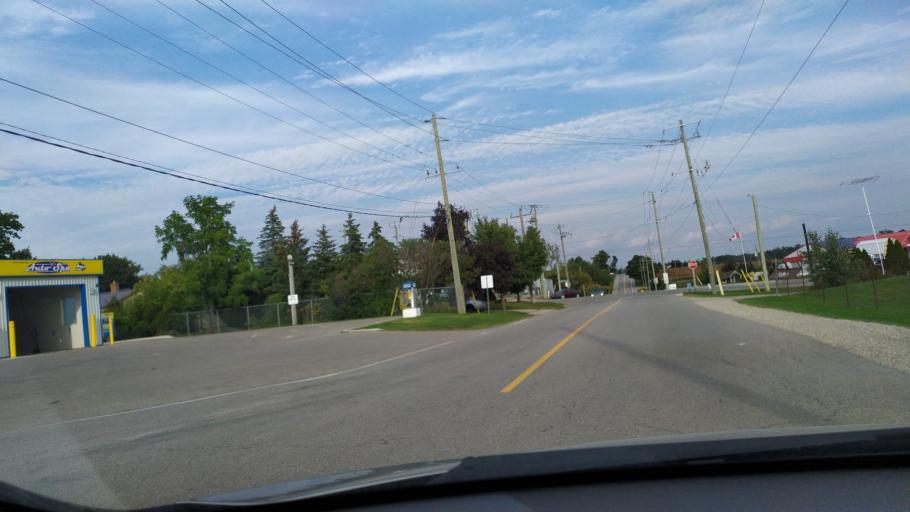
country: CA
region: Ontario
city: Stratford
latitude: 43.4700
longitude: -80.7663
